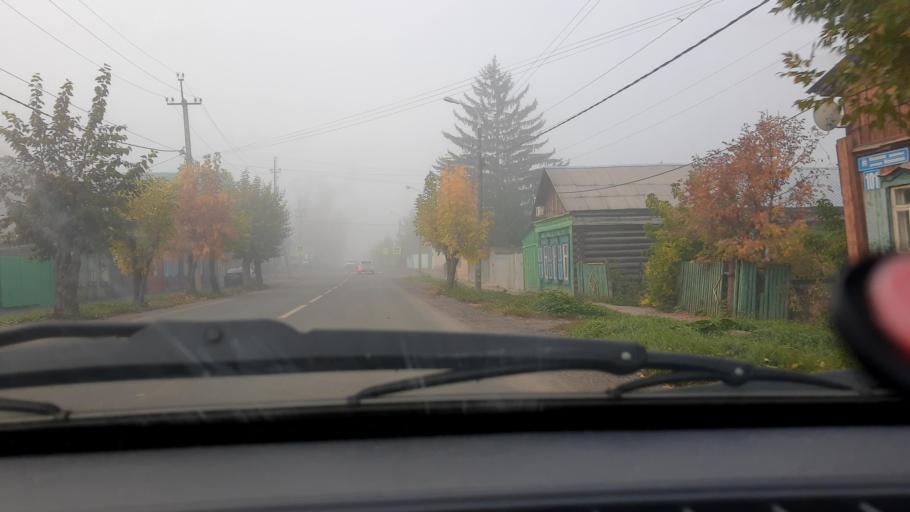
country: RU
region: Bashkortostan
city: Ufa
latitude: 54.7353
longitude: 55.9183
